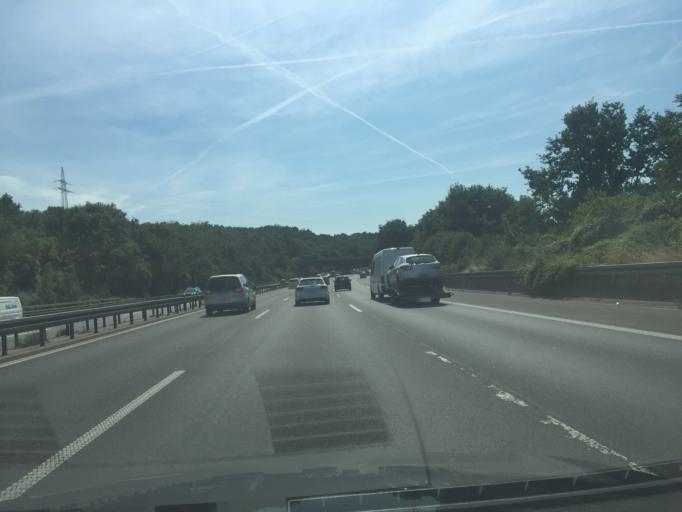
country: DE
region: North Rhine-Westphalia
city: Schwerte
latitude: 51.4126
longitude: 7.5512
